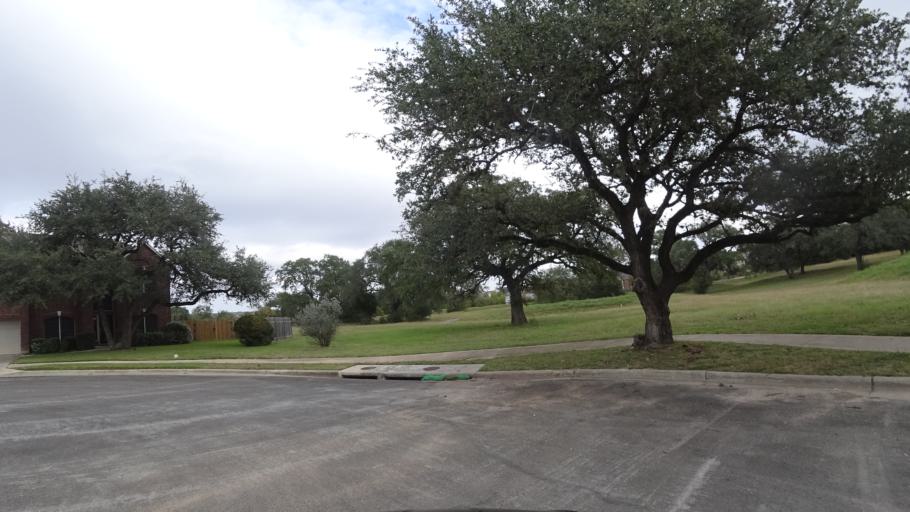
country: US
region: Texas
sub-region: Travis County
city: Shady Hollow
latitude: 30.1584
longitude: -97.8473
